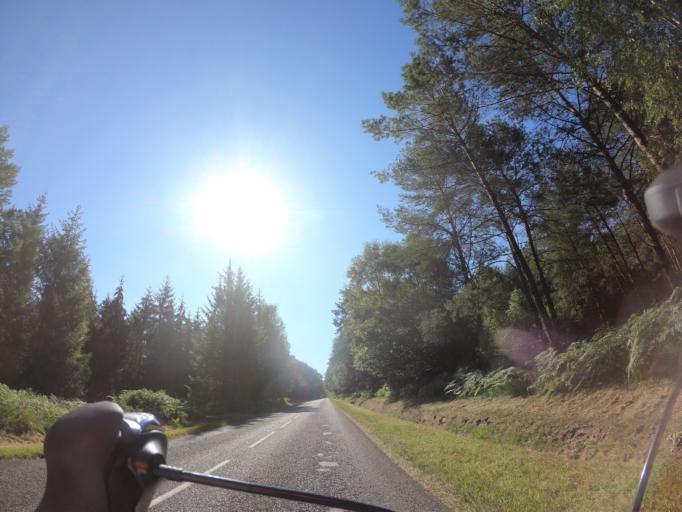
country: FR
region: Lower Normandy
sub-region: Departement de l'Orne
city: Juvigny-sous-Andaine
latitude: 48.5810
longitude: -0.4737
